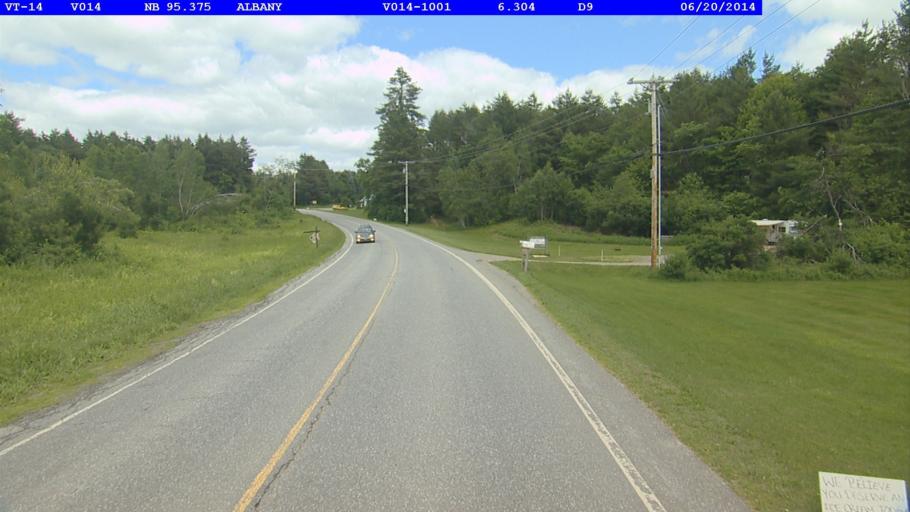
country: US
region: Vermont
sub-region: Orleans County
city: Newport
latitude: 44.7724
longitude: -72.3232
